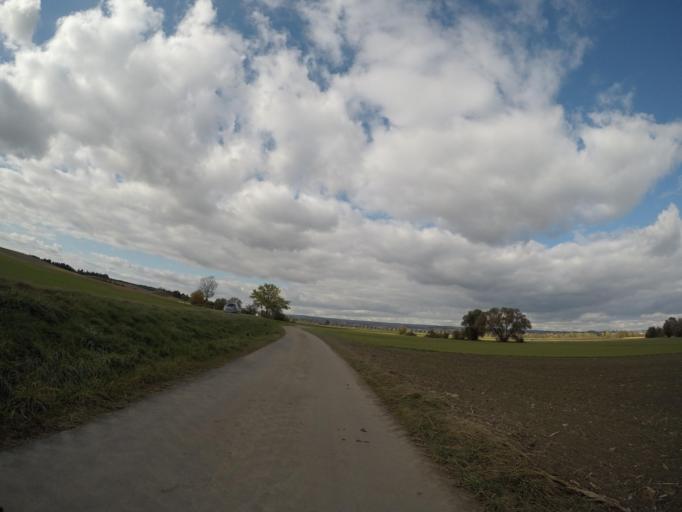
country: DE
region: Baden-Wuerttemberg
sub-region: Tuebingen Region
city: Unterstadion
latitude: 48.2071
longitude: 9.6796
